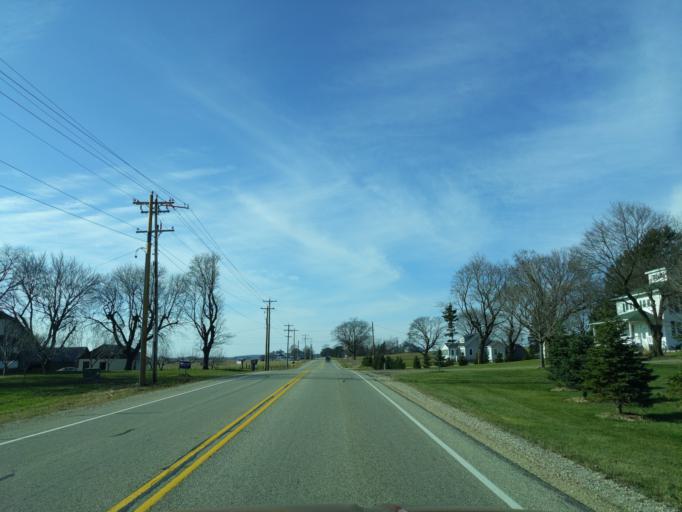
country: US
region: Wisconsin
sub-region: Walworth County
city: Elkhorn
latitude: 42.7350
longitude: -88.5880
